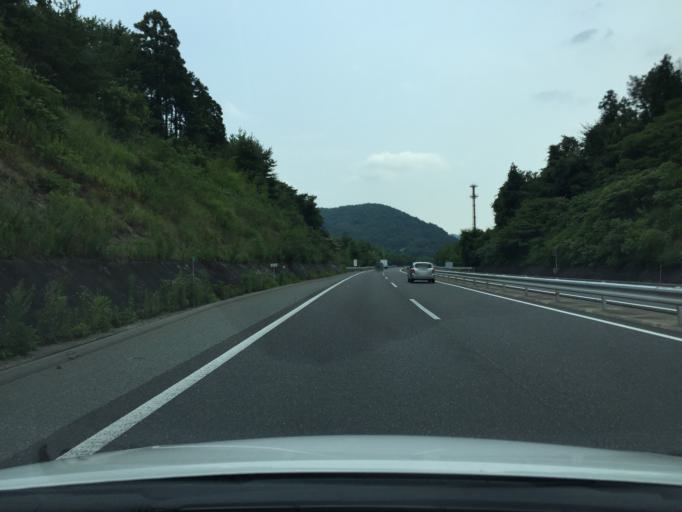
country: JP
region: Fukushima
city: Iwaki
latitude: 37.0546
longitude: 140.8022
